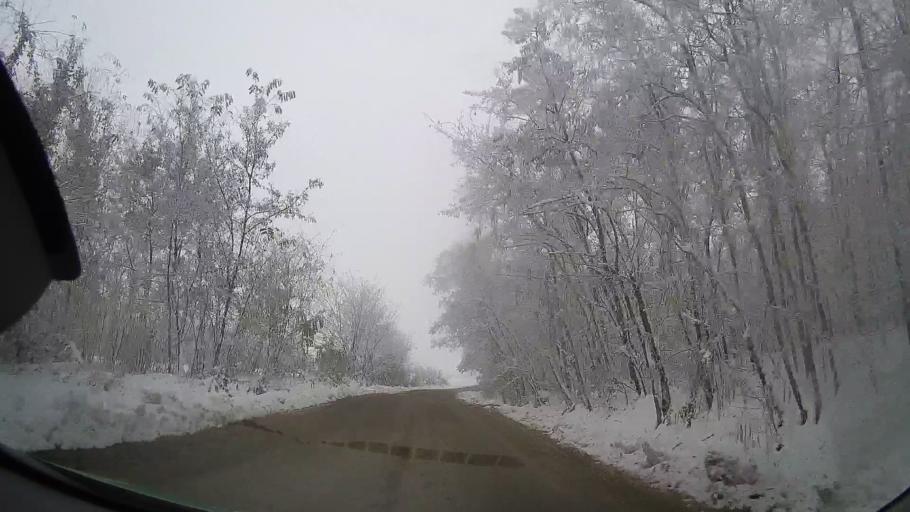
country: RO
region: Iasi
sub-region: Comuna Tansa
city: Suhulet
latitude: 46.8972
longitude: 27.2453
